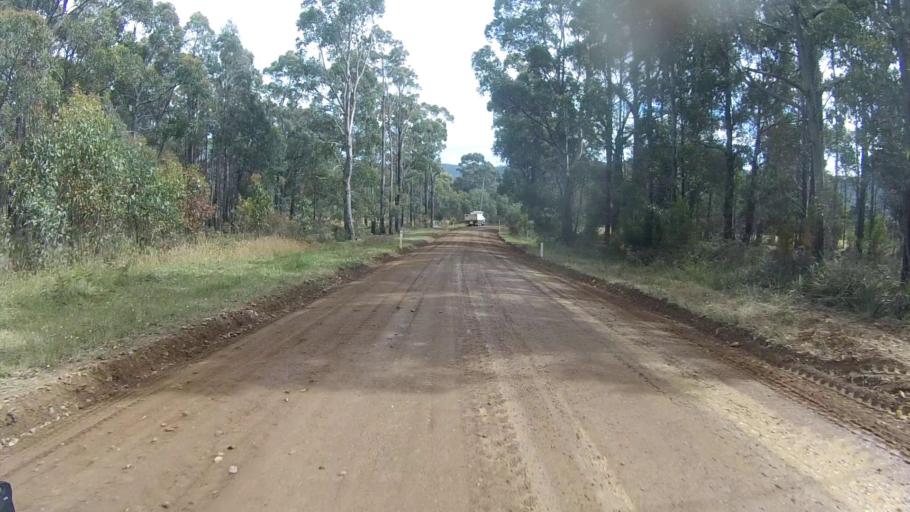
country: AU
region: Tasmania
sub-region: Sorell
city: Sorell
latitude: -42.7770
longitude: 147.8089
